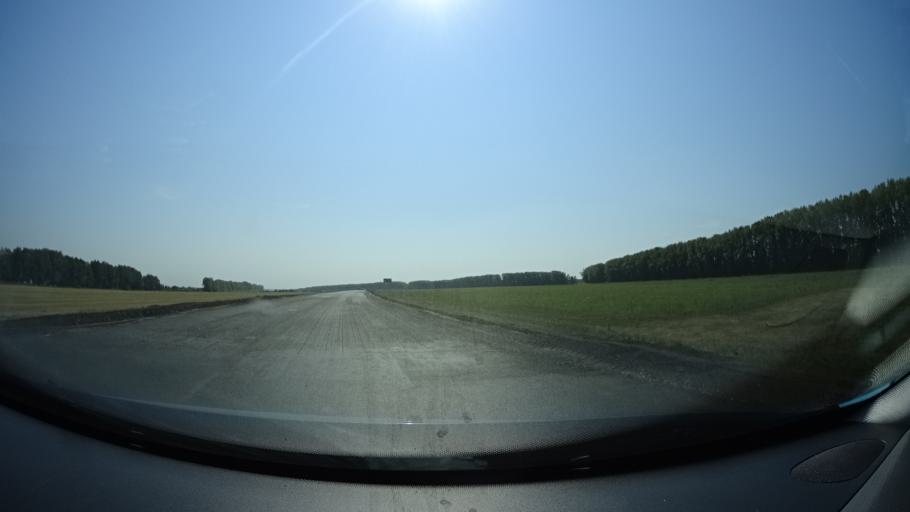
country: RU
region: Bashkortostan
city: Kabakovo
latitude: 54.4630
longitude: 55.9622
